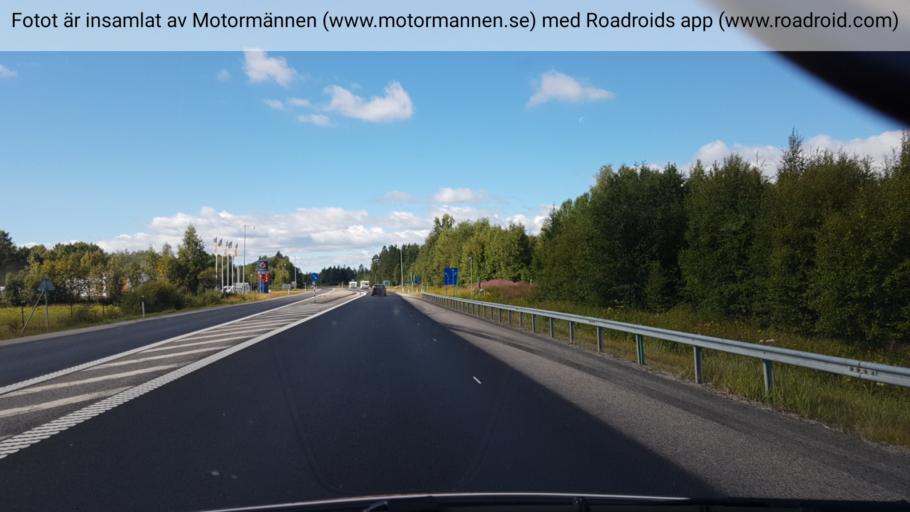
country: SE
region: Vaesterbotten
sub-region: Umea Kommun
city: Hoernefors
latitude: 63.6393
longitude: 19.9151
